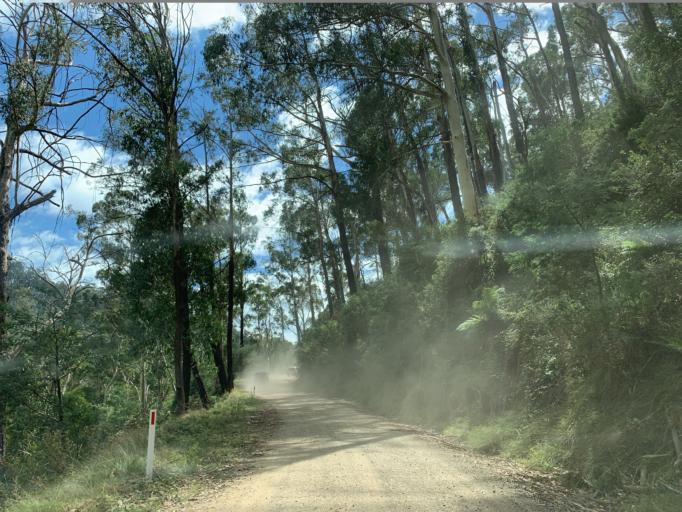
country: AU
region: Victoria
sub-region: Mansfield
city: Mansfield
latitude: -37.1021
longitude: 146.5044
